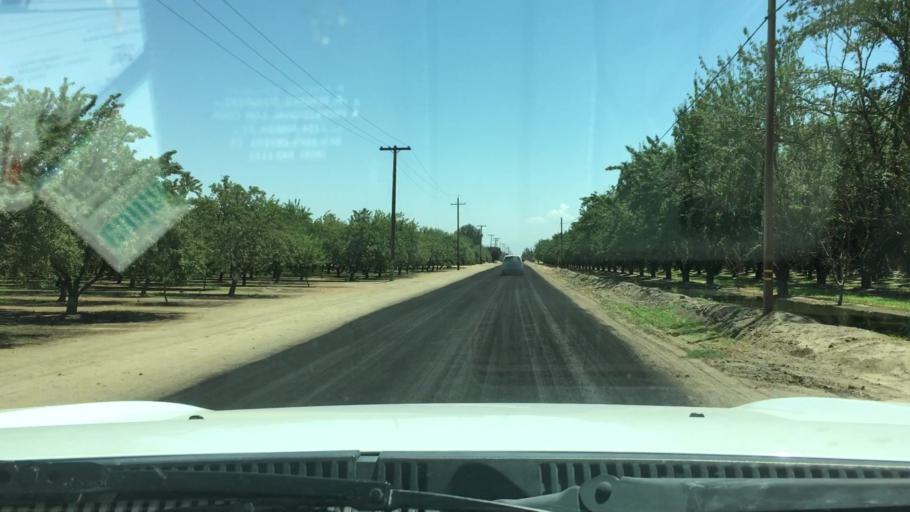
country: US
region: California
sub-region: Kern County
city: Shafter
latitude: 35.5291
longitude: -119.3221
